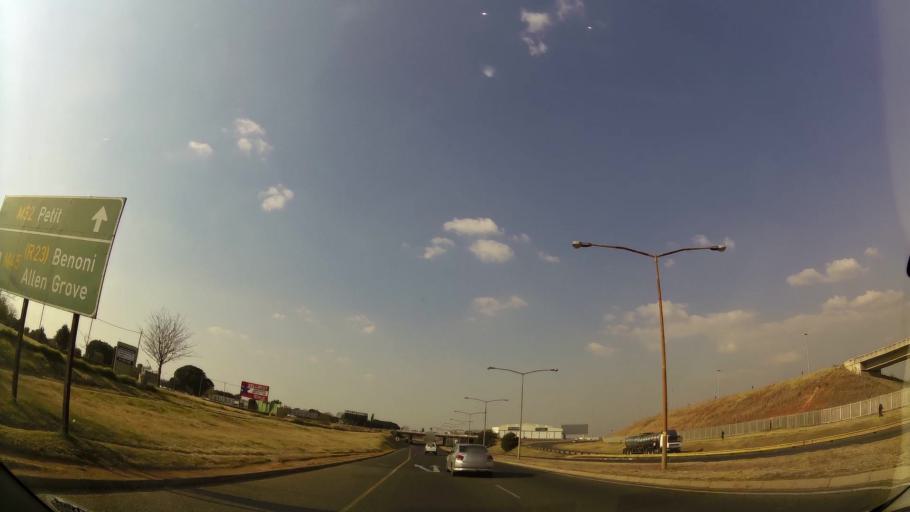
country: ZA
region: Gauteng
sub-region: City of Johannesburg Metropolitan Municipality
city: Modderfontein
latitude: -26.1009
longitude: 28.2503
